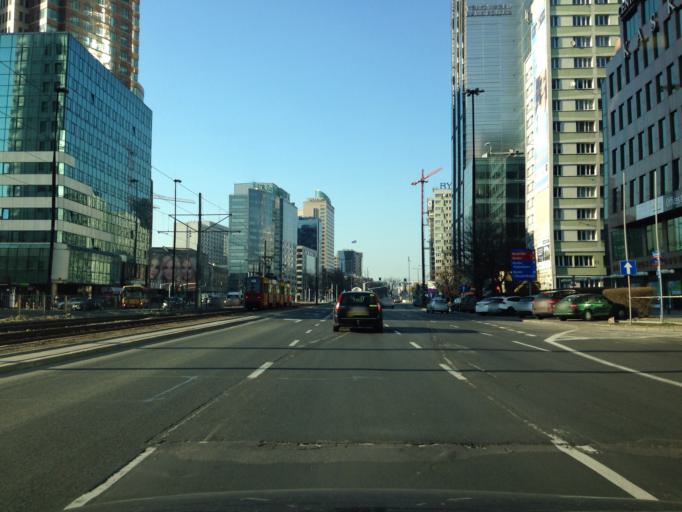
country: PL
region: Masovian Voivodeship
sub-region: Warszawa
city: Warsaw
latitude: 52.2313
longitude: 20.9997
